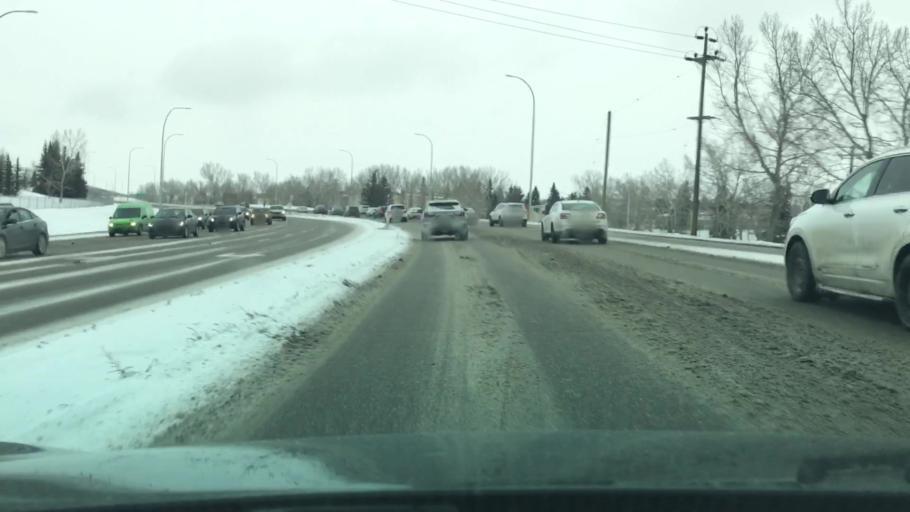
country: CA
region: Alberta
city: Calgary
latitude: 51.1033
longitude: -114.1425
